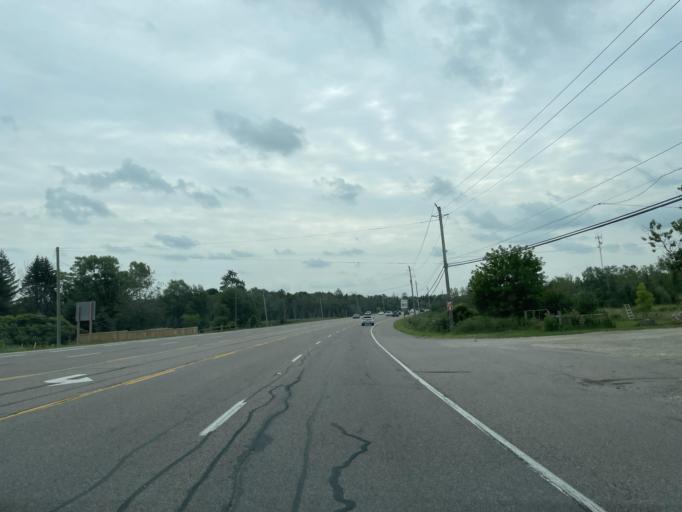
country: CA
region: Ontario
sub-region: Halton
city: Milton
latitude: 43.4187
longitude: -80.0642
